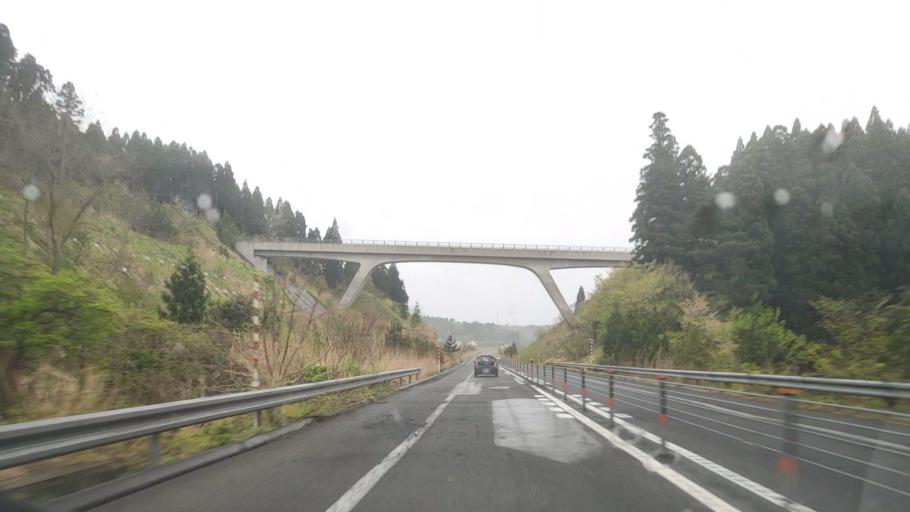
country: JP
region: Akita
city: Noshiromachi
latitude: 40.1899
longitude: 140.1043
